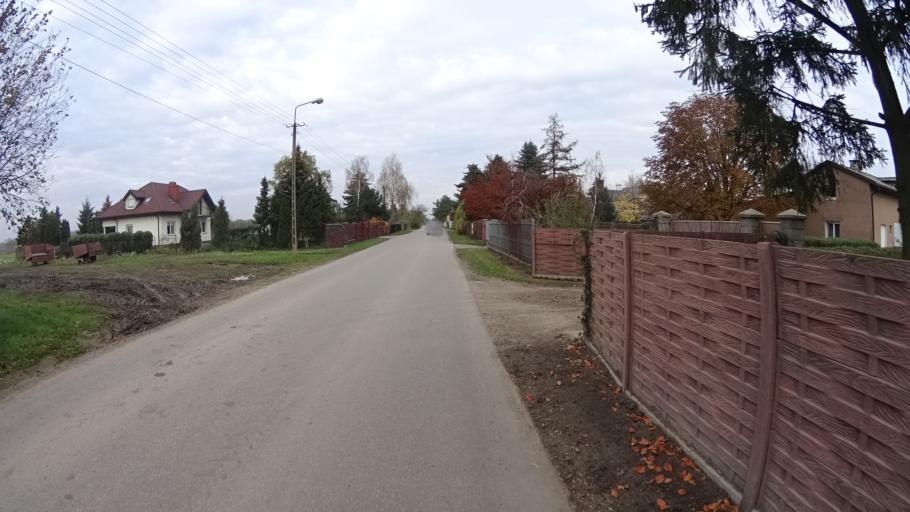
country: PL
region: Masovian Voivodeship
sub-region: Powiat warszawski zachodni
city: Stare Babice
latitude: 52.2385
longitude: 20.8282
